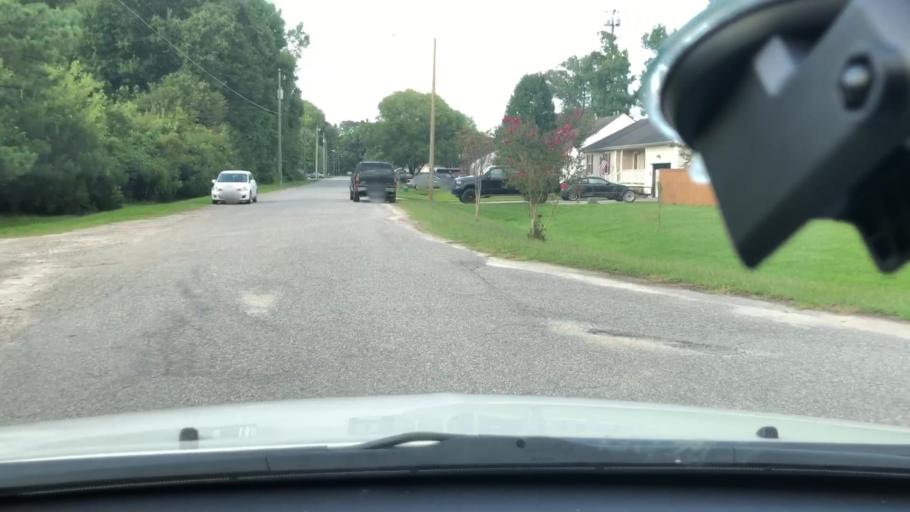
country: US
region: Virginia
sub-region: City of Chesapeake
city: Chesapeake
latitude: 36.7193
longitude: -76.2714
